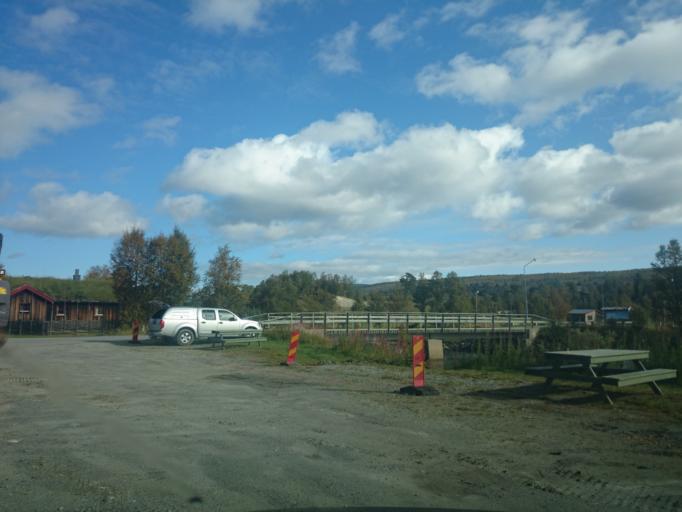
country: NO
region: Sor-Trondelag
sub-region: Tydal
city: Aas
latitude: 62.6411
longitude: 12.4178
